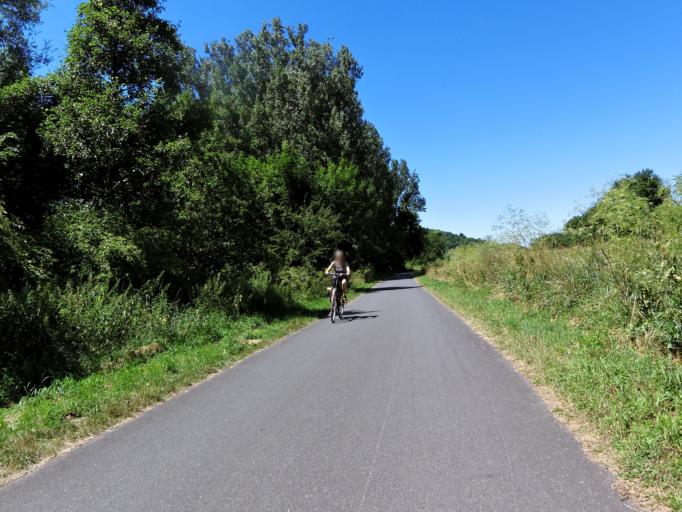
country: DE
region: Bavaria
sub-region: Regierungsbezirk Unterfranken
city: Sommerhausen
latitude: 49.6860
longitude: 10.0286
